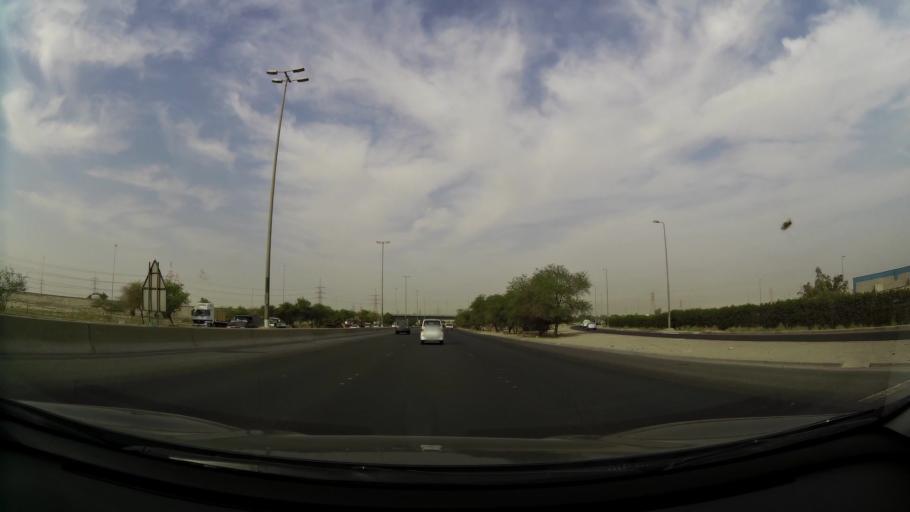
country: KW
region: Al Asimah
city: Ar Rabiyah
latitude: 29.2651
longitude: 47.8435
